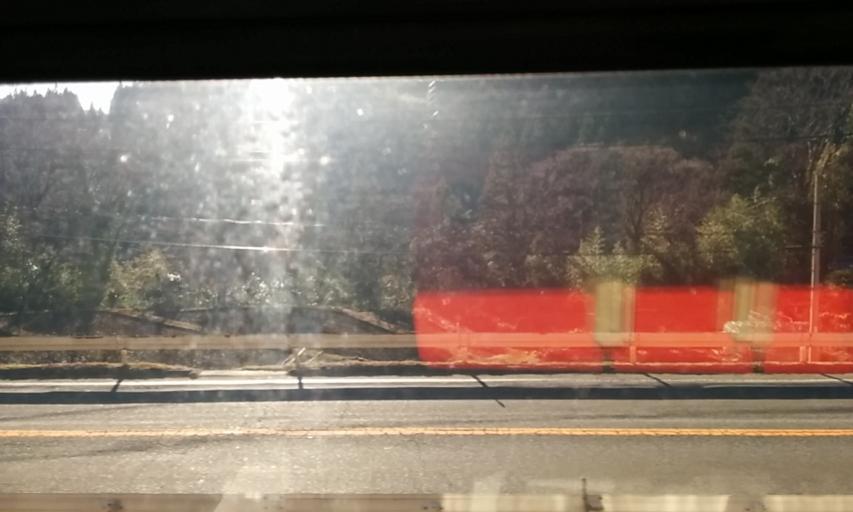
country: JP
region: Nagano
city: Iida
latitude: 35.7271
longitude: 137.7141
